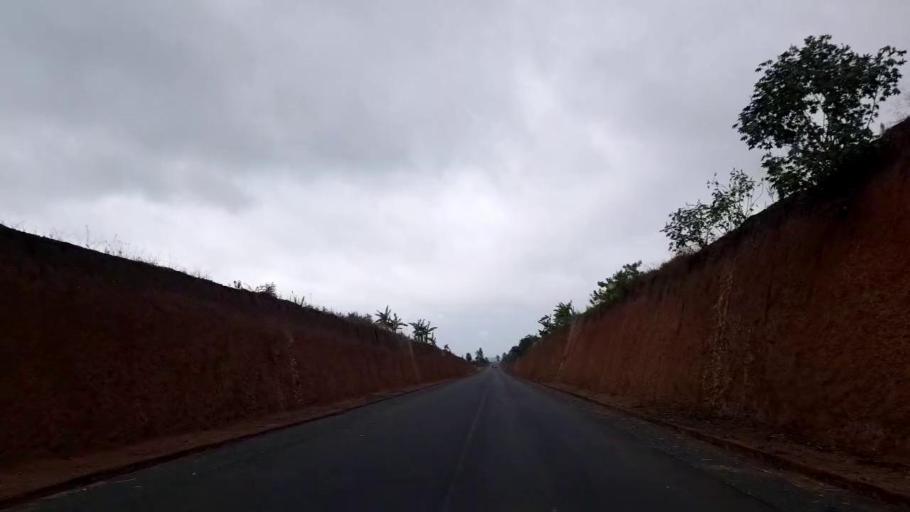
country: RW
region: Northern Province
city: Byumba
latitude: -1.4313
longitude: 30.2626
